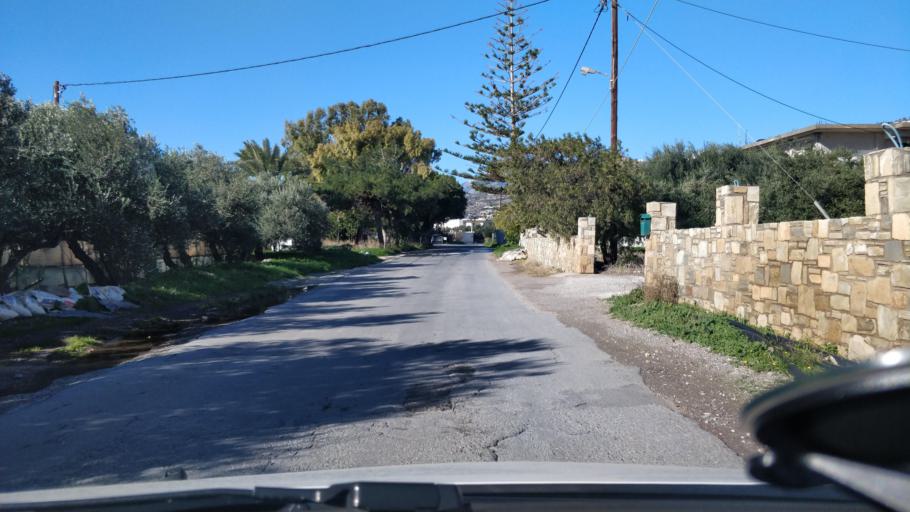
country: GR
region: Crete
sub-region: Nomos Lasithiou
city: Gra Liyia
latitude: 35.0202
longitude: 25.6803
